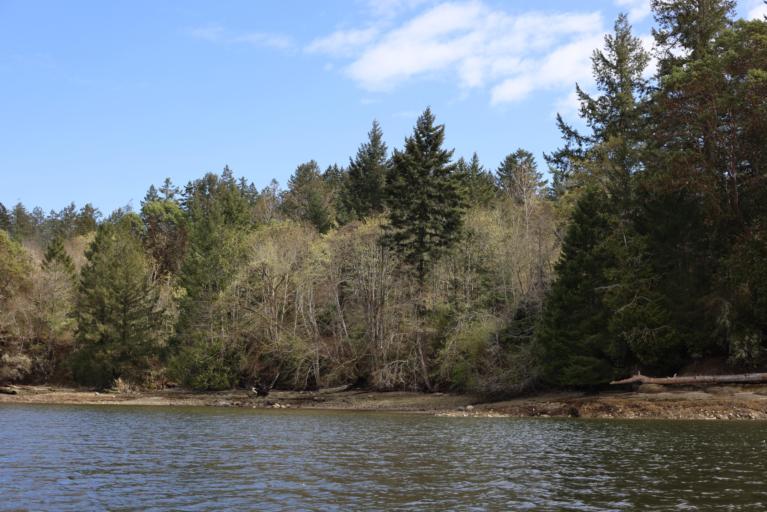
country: CA
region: British Columbia
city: North Saanich
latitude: 48.6263
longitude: -123.4673
